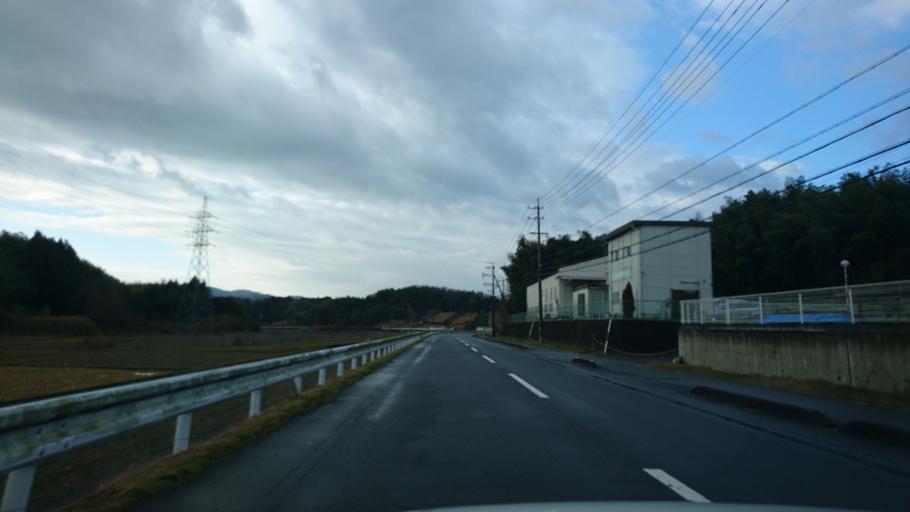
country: JP
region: Mie
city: Ueno-ebisumachi
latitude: 34.7212
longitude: 136.0795
